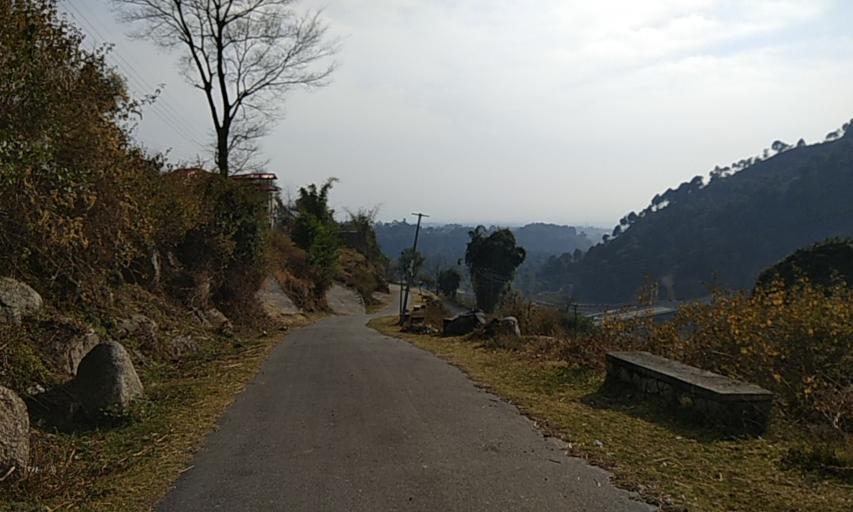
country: IN
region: Himachal Pradesh
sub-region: Kangra
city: Palampur
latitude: 32.1364
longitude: 76.5356
